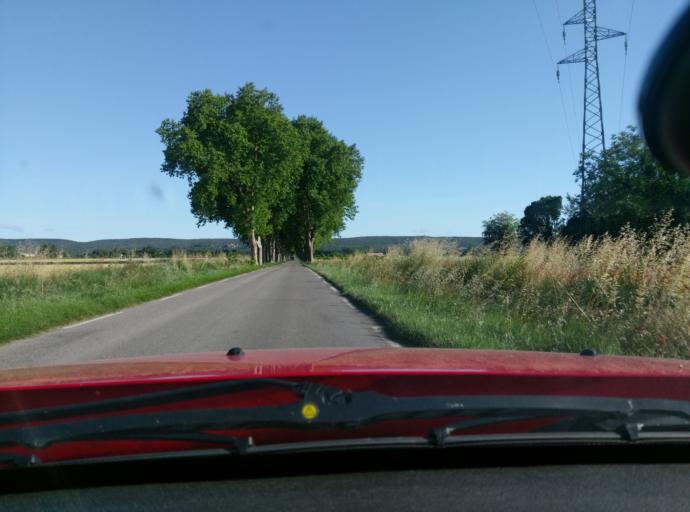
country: FR
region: Languedoc-Roussillon
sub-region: Departement du Gard
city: Uzes
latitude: 44.0339
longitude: 4.4098
